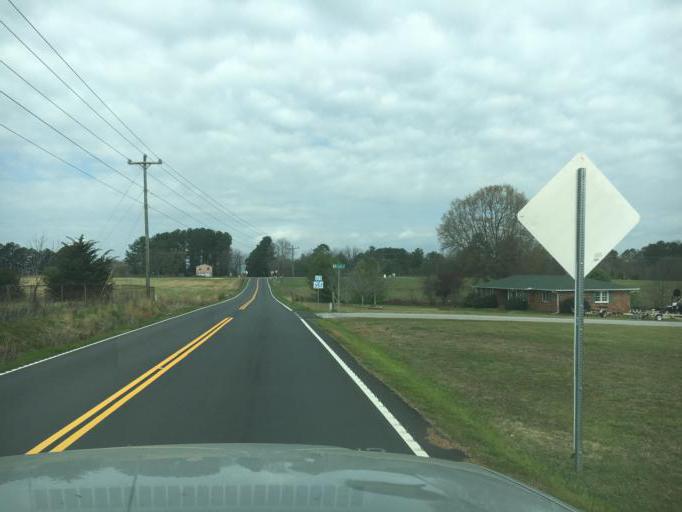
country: US
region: South Carolina
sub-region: Spartanburg County
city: Inman Mills
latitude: 35.0666
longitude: -82.1720
